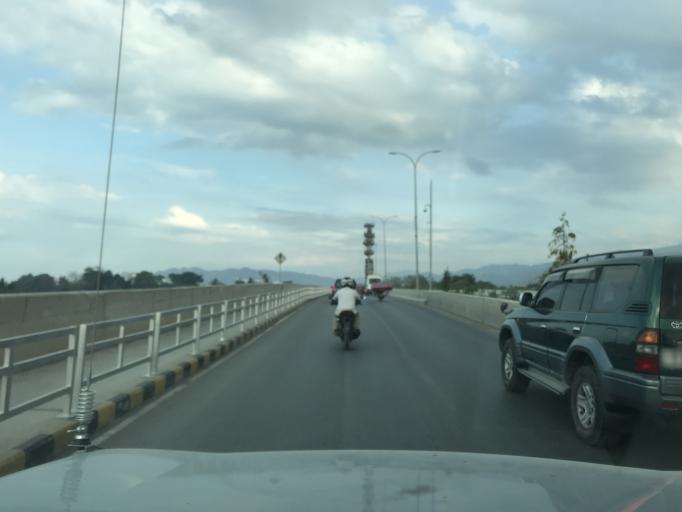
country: TL
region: Dili
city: Dili
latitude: -8.5539
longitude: 125.5351
